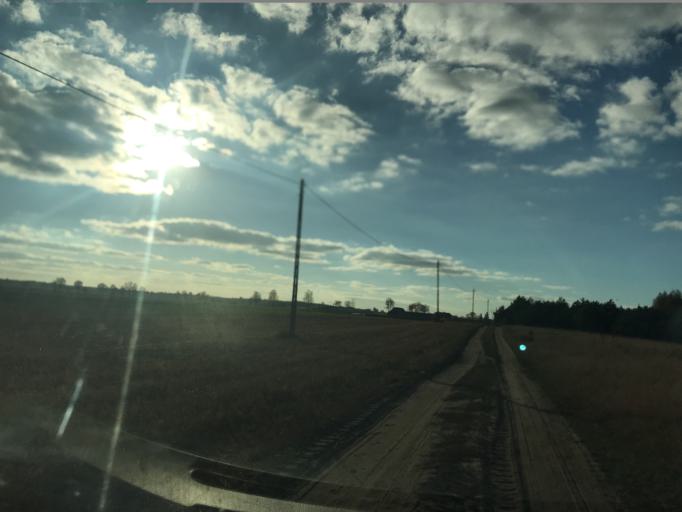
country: PL
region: Warmian-Masurian Voivodeship
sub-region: Powiat dzialdowski
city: Lidzbark
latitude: 53.3691
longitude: 19.8266
